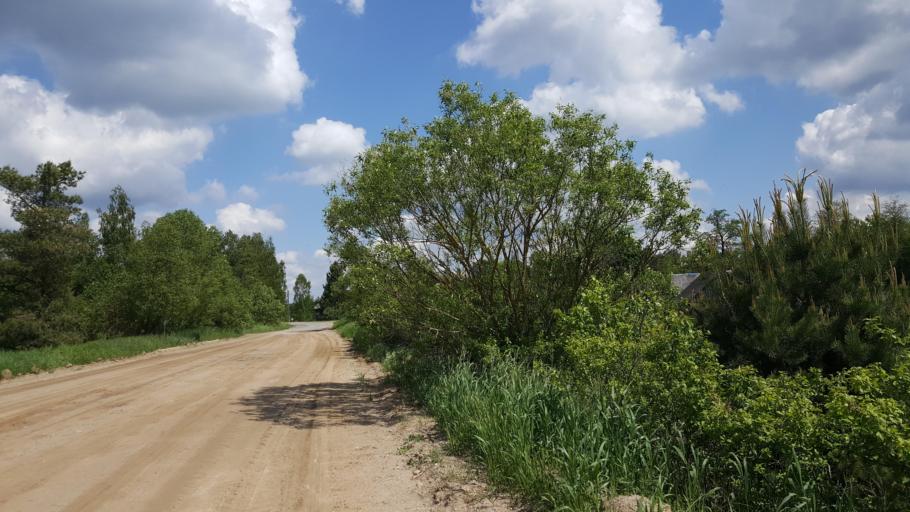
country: BY
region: Brest
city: Kamyanyets
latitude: 52.4419
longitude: 23.9784
